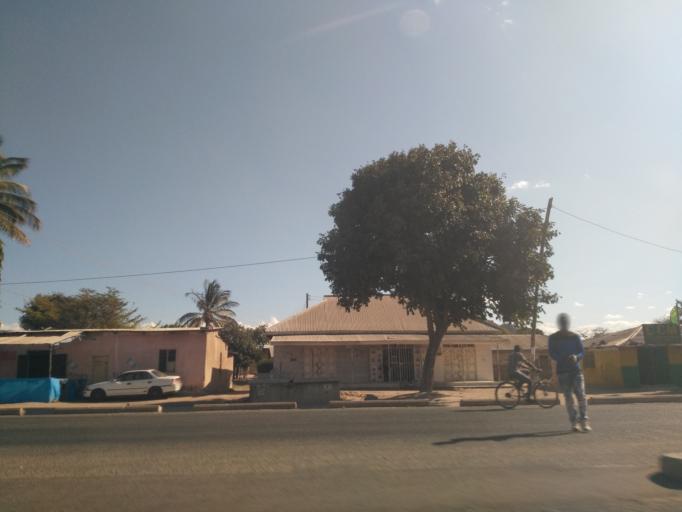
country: TZ
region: Dodoma
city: Dodoma
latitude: -6.1686
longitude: 35.7262
